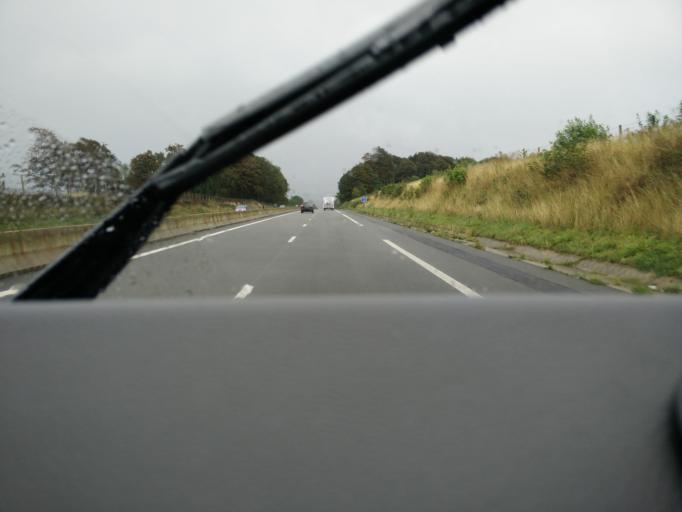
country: FR
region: Nord-Pas-de-Calais
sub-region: Departement du Pas-de-Calais
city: Marconnelle
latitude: 50.3615
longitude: 1.9952
